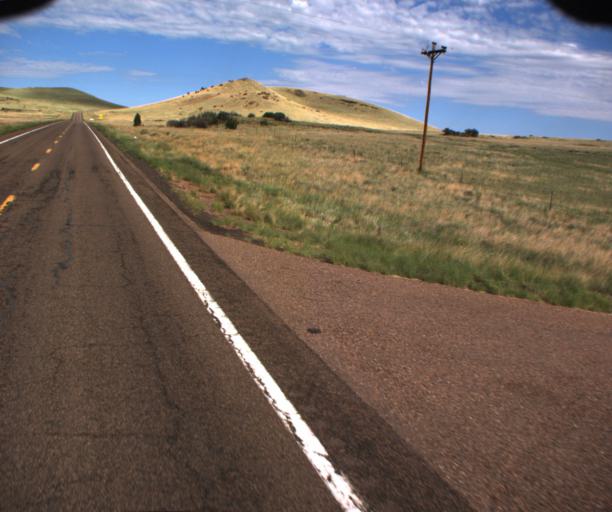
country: US
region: Arizona
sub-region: Apache County
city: Springerville
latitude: 34.2043
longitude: -109.4109
